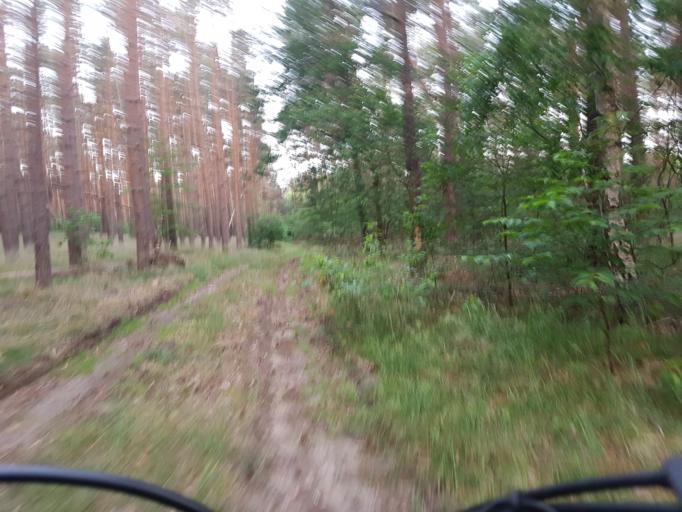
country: DE
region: Brandenburg
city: Schilda
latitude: 51.5682
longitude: 13.3607
